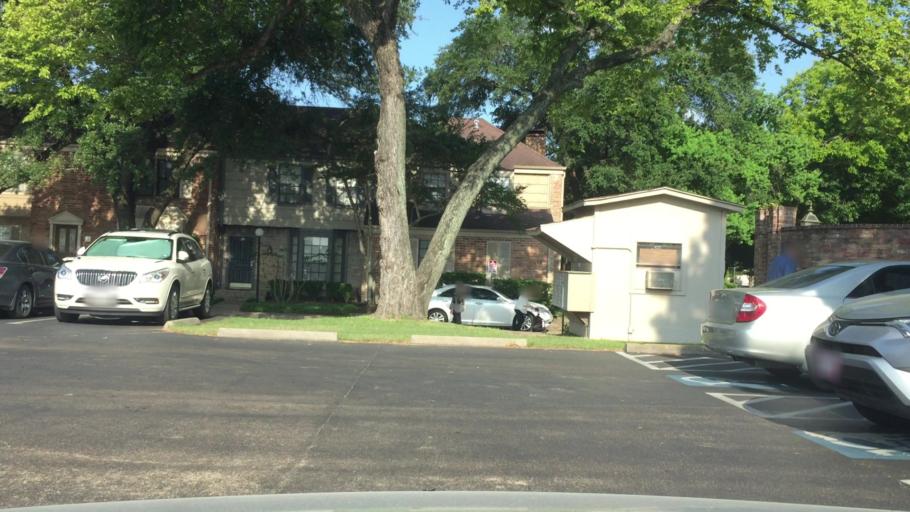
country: US
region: Texas
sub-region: Harris County
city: Hunters Creek Village
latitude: 29.7817
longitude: -95.4602
